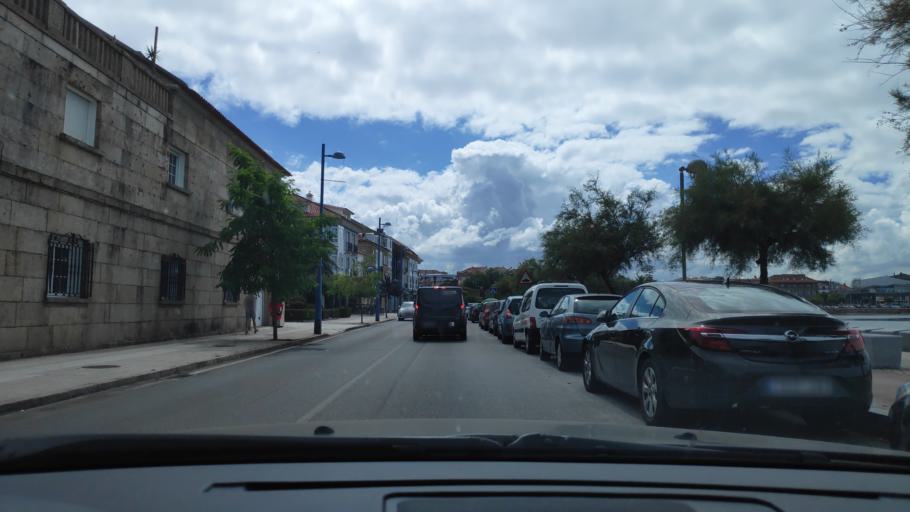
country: ES
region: Galicia
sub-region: Provincia de Pontevedra
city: Cambados
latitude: 42.5184
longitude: -8.8167
